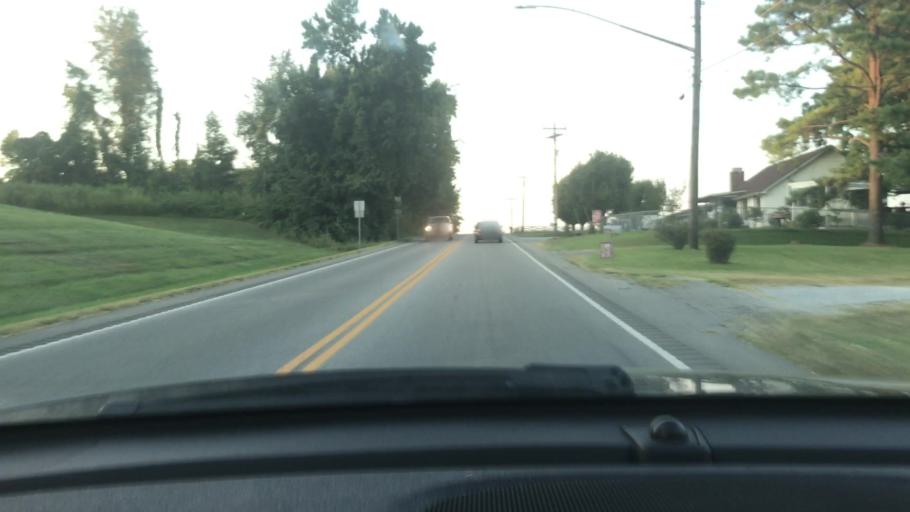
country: US
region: Tennessee
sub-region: Dickson County
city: Dickson
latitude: 36.0864
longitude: -87.3781
